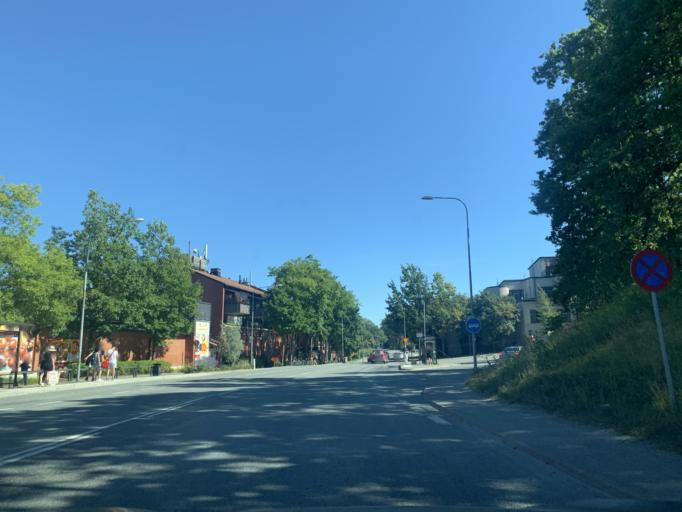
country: SE
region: Stockholm
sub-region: Ekero Kommun
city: Ekeroe
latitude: 59.2902
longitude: 17.8101
